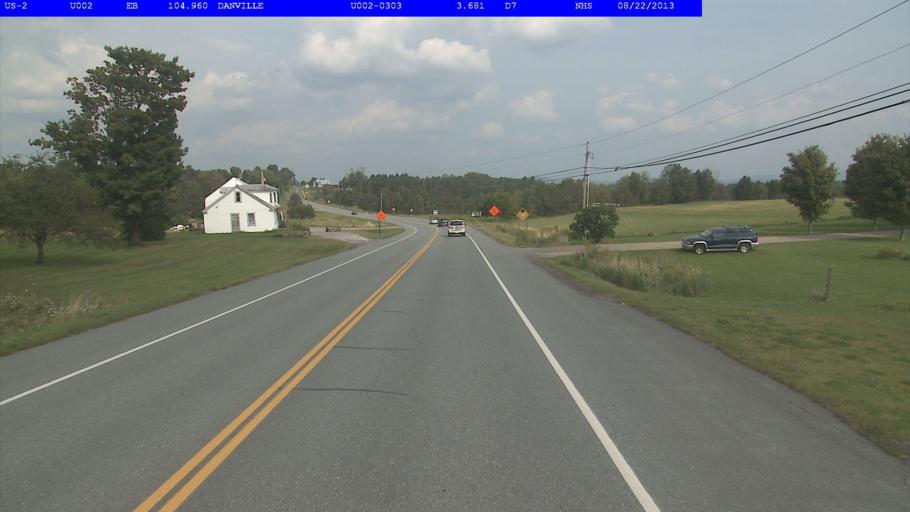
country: US
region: Vermont
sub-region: Caledonia County
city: Saint Johnsbury
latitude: 44.4100
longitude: -72.1556
